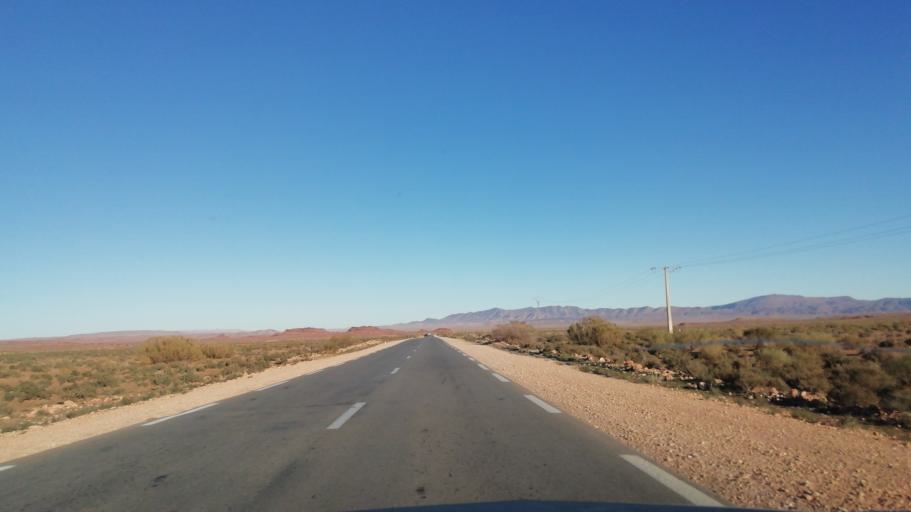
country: DZ
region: El Bayadh
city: El Abiodh Sidi Cheikh
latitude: 33.1687
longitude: 0.4784
